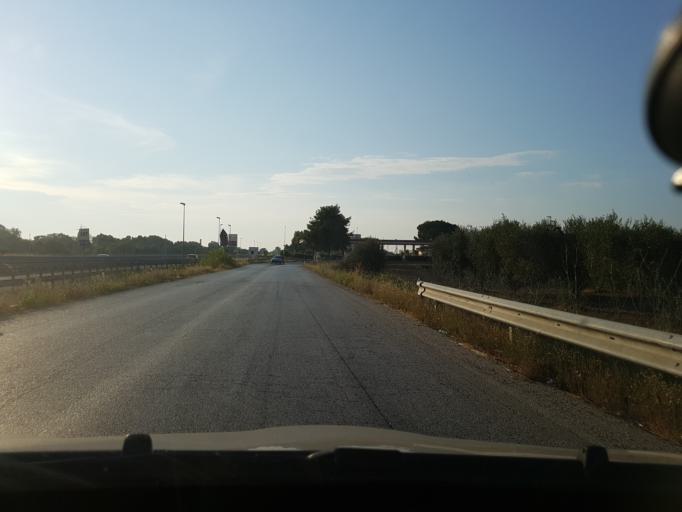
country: IT
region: Apulia
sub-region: Provincia di Foggia
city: Carapelle
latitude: 41.3965
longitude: 15.6580
